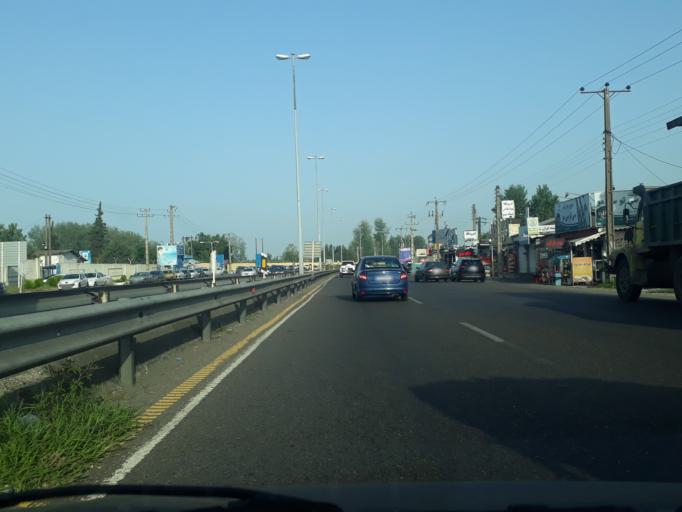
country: IR
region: Gilan
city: Bandar-e Anzali
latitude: 37.4574
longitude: 49.6102
